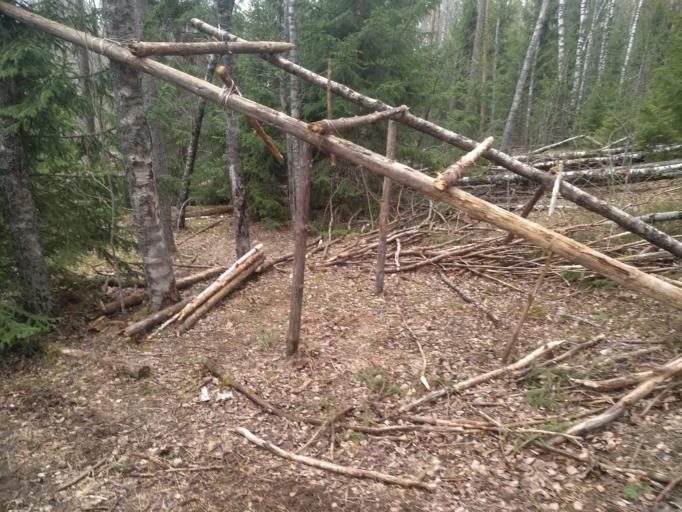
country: RU
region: Leningrad
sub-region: Vsevolzhskij Rajon
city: Vaskelovo
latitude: 60.4466
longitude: 30.3290
